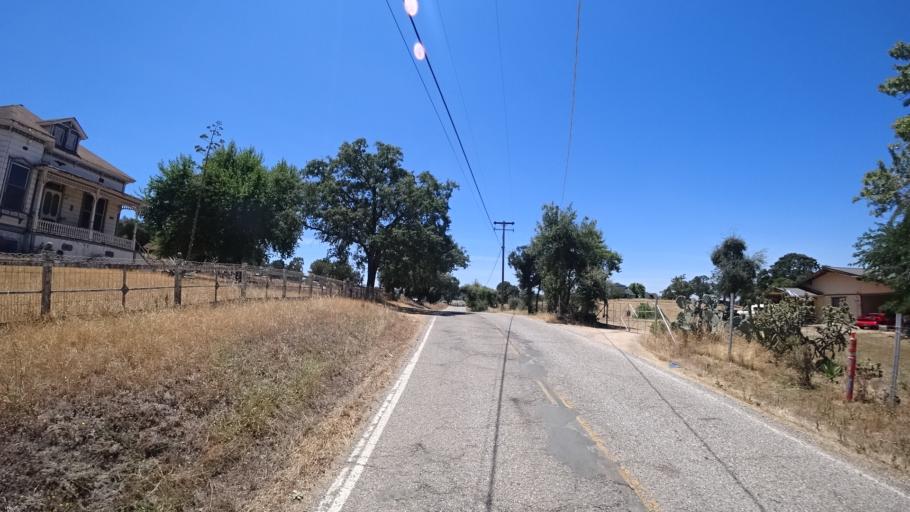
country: US
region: California
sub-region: Calaveras County
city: Valley Springs
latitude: 38.2248
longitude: -120.8552
